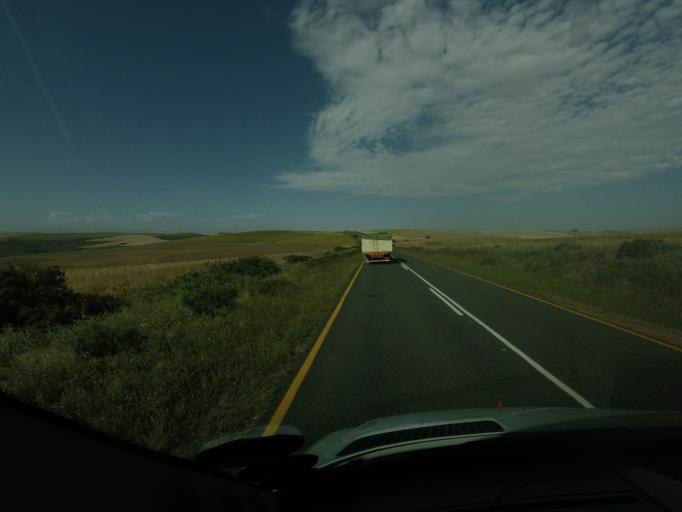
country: ZA
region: Western Cape
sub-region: Overberg District Municipality
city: Caledon
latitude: -34.3342
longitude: 19.7150
